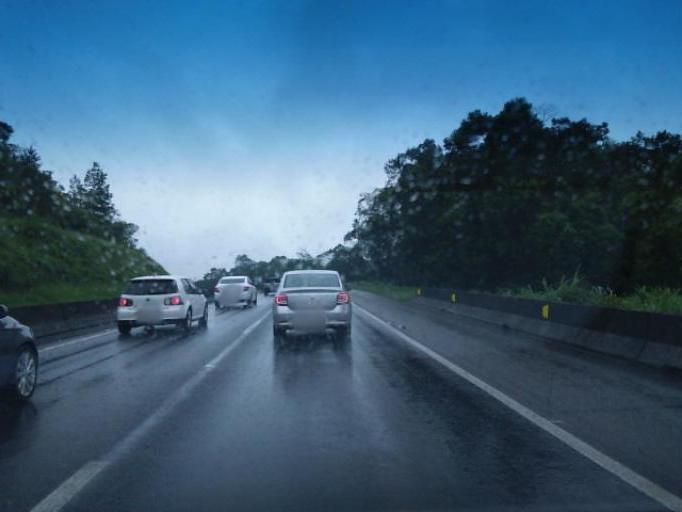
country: BR
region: Santa Catarina
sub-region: Joinville
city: Joinville
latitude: -26.1304
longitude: -48.8916
